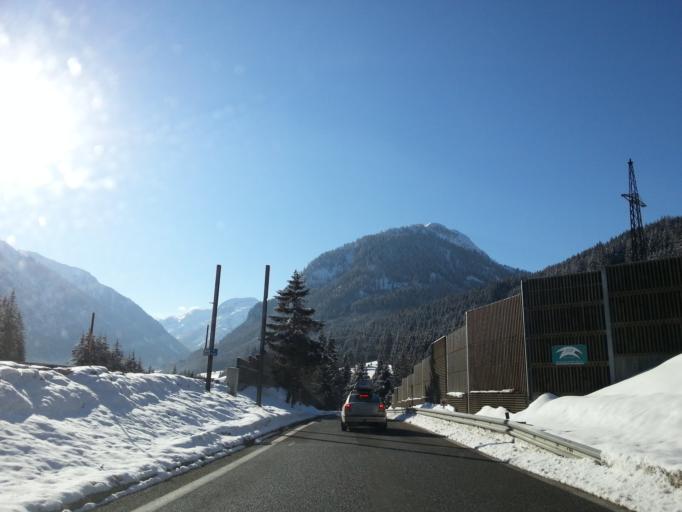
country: AT
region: Salzburg
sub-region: Politischer Bezirk Sankt Johann im Pongau
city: Flachau
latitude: 47.2978
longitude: 13.3929
